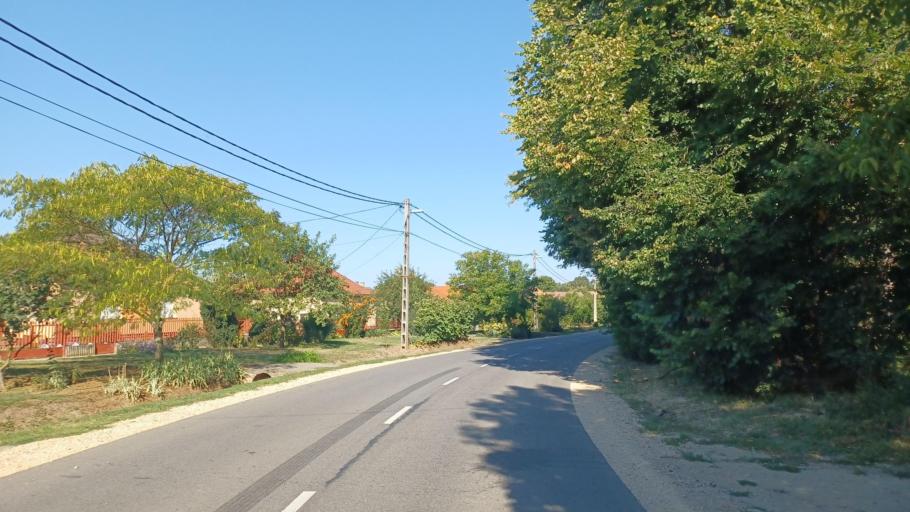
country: HU
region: Tolna
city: Nemetker
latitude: 46.6778
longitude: 18.8092
